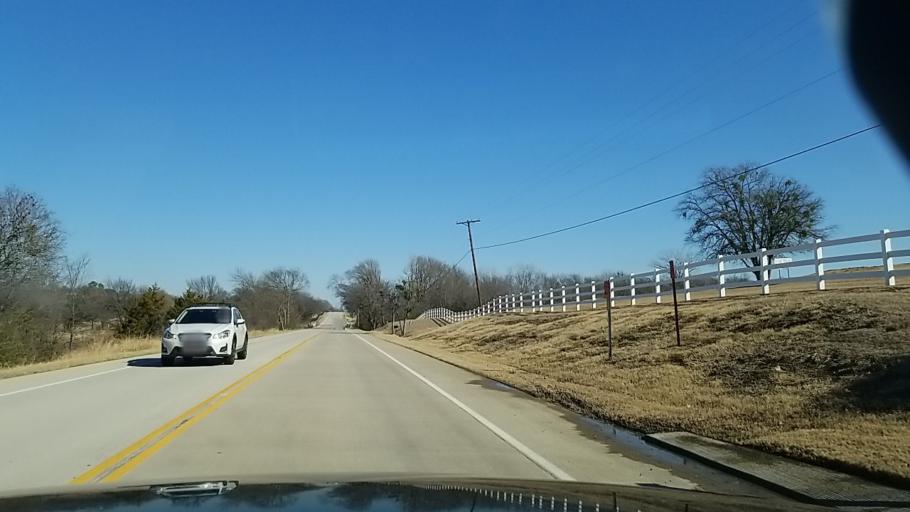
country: US
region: Texas
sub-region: Denton County
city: Argyle
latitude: 33.1363
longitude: -97.1648
